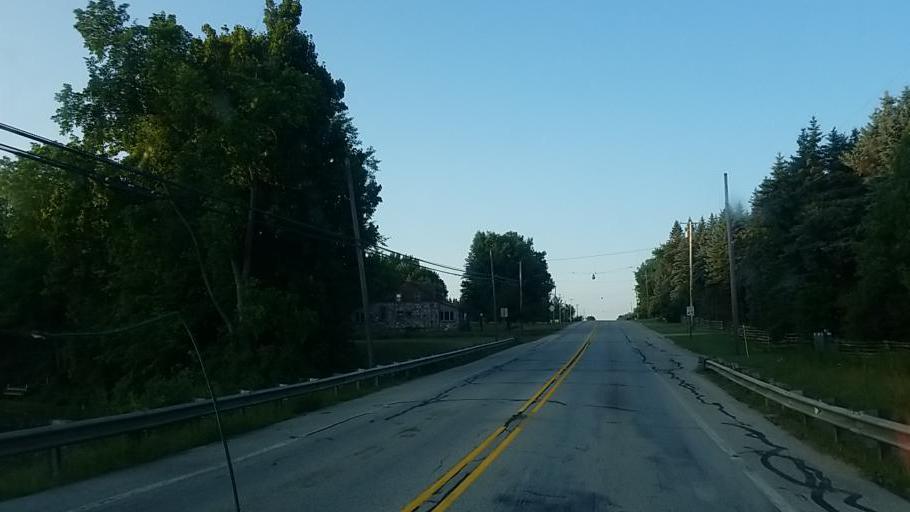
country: US
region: Michigan
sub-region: Isabella County
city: Lake Isabella
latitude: 43.7464
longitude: -85.1474
